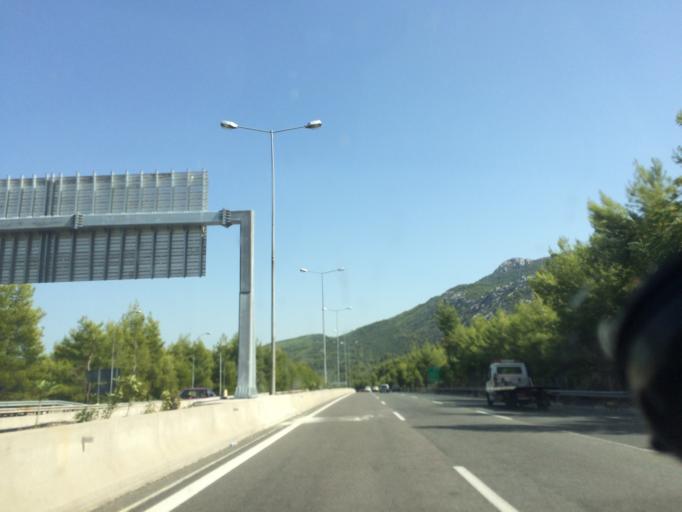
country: GR
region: Attica
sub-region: Nomarchia Anatolikis Attikis
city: Afidnes
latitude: 38.2349
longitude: 23.7893
